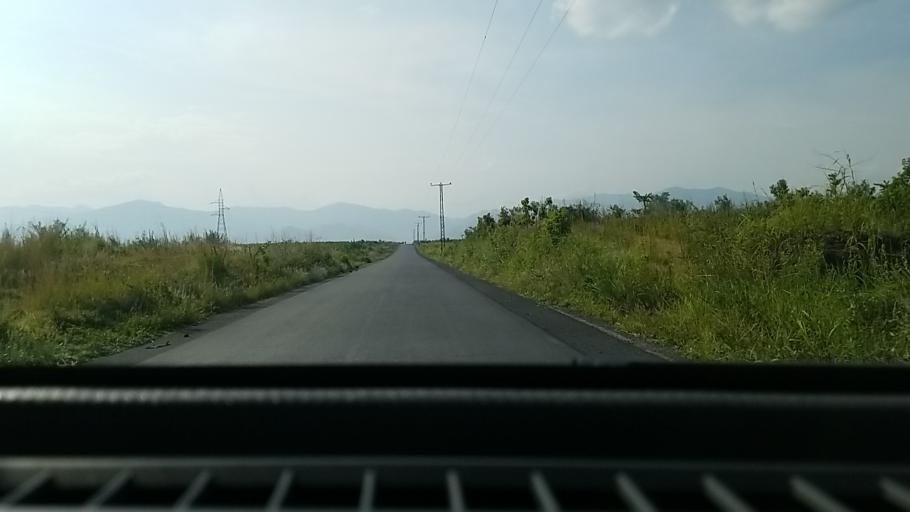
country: CD
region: Nord Kivu
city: Sake
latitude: -1.5964
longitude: 29.1062
